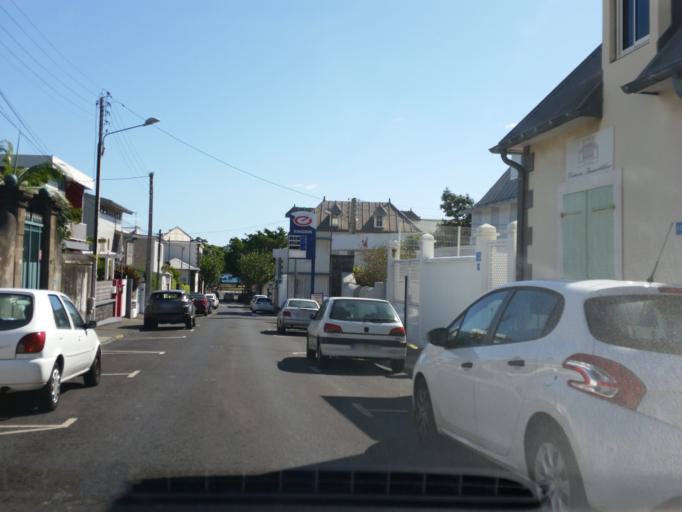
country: RE
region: Reunion
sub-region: Reunion
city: Saint-Denis
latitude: -20.8746
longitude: 55.4488
